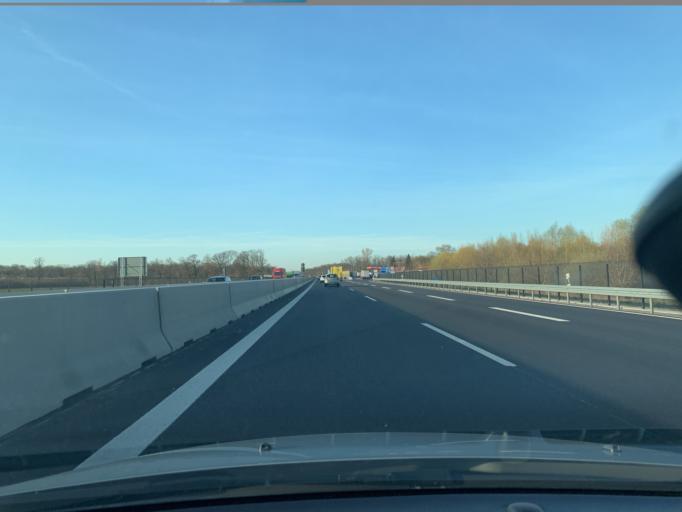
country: DE
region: Baden-Wuerttemberg
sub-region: Freiburg Region
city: Mahlberg
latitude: 48.3040
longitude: 7.7902
